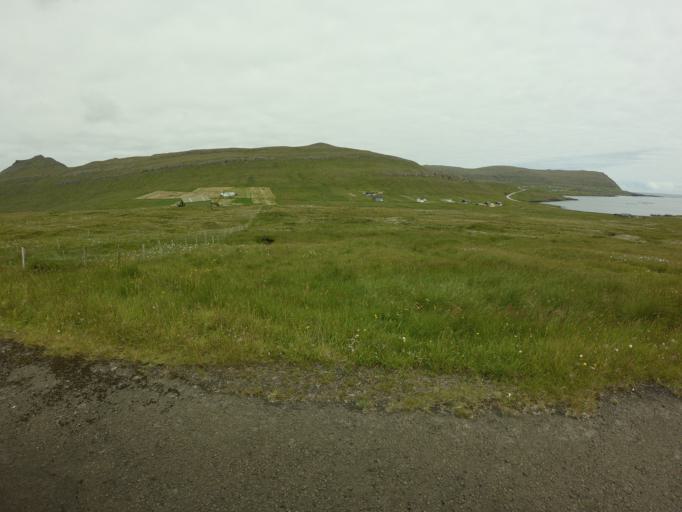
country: FO
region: Suduroy
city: Tvoroyri
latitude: 61.5310
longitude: -6.8240
